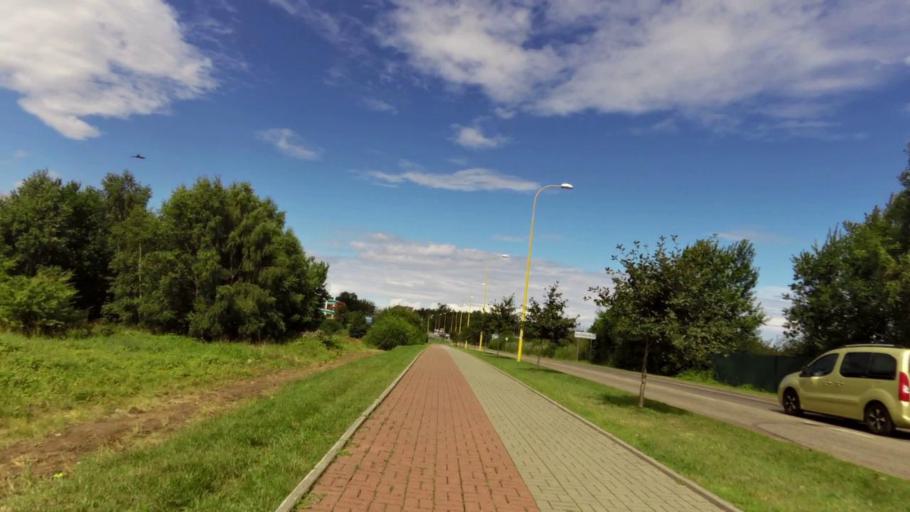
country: PL
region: West Pomeranian Voivodeship
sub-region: Powiat slawienski
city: Darlowo
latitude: 54.4435
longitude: 16.4002
